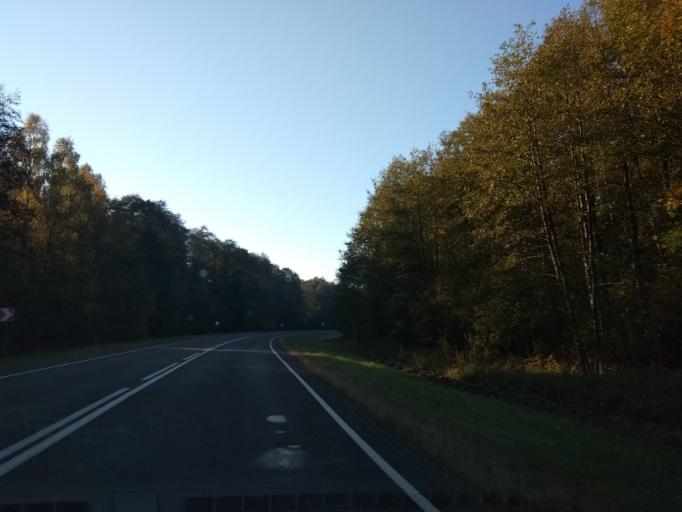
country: BY
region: Brest
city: Kobryn
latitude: 52.0667
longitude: 24.2842
